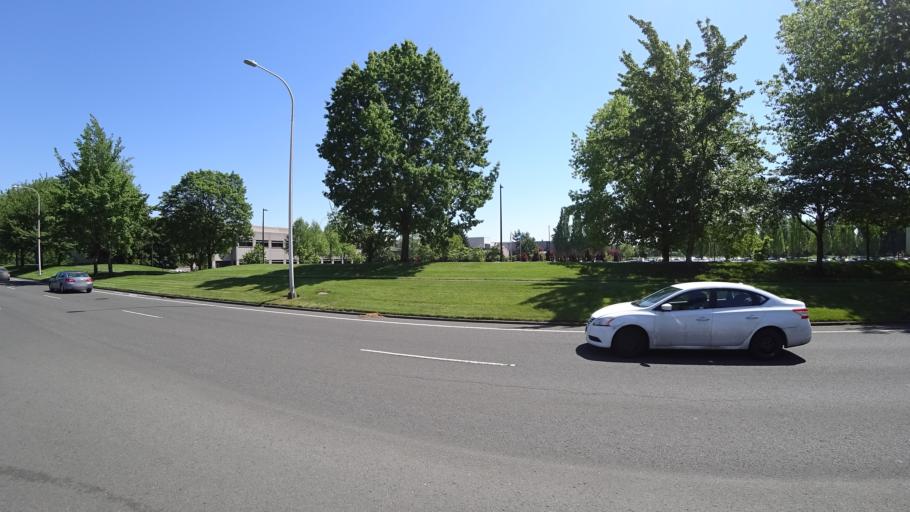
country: US
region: Oregon
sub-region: Washington County
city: Rockcreek
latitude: 45.5337
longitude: -122.9293
